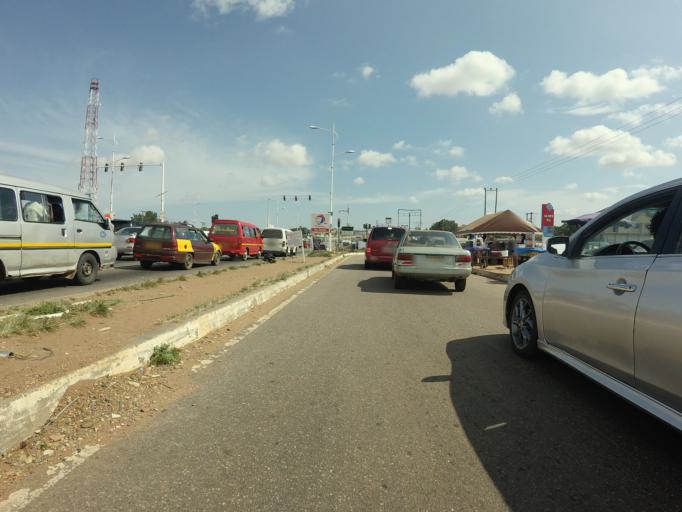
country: GH
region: Greater Accra
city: Medina Estates
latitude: 5.6869
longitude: -0.1716
